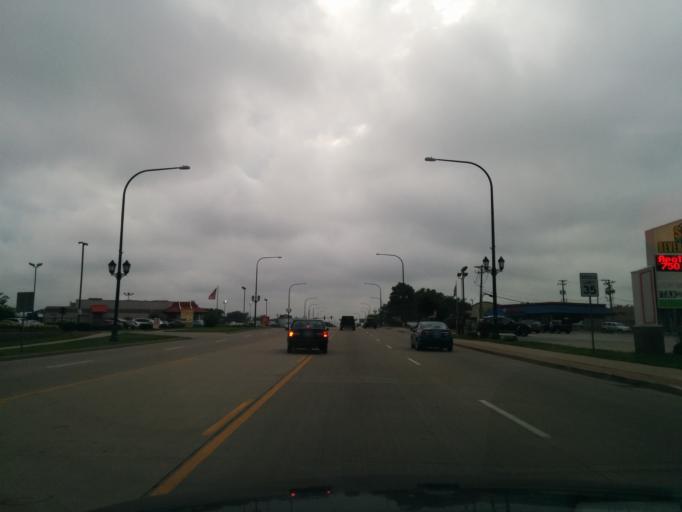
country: US
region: Illinois
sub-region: DuPage County
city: Addison
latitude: 41.9368
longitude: -87.9993
